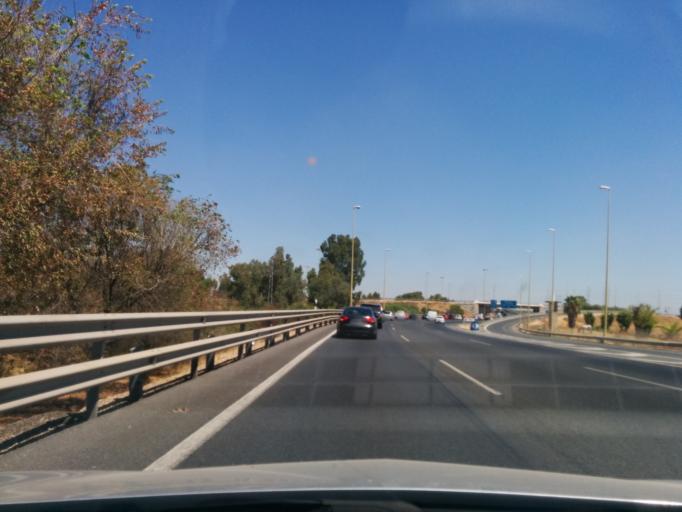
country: ES
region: Andalusia
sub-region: Provincia de Sevilla
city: Camas
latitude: 37.3848
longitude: -6.0256
